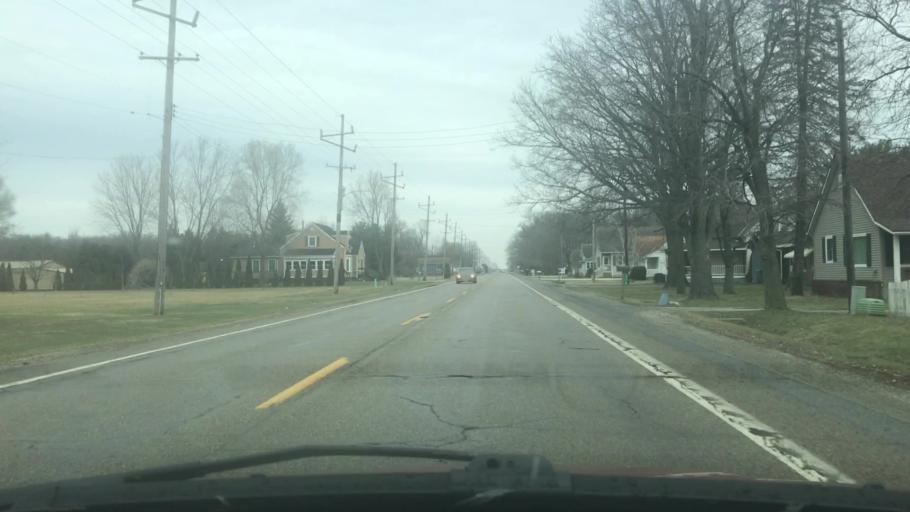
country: US
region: Indiana
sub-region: Porter County
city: Kouts
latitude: 41.3212
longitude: -87.0258
